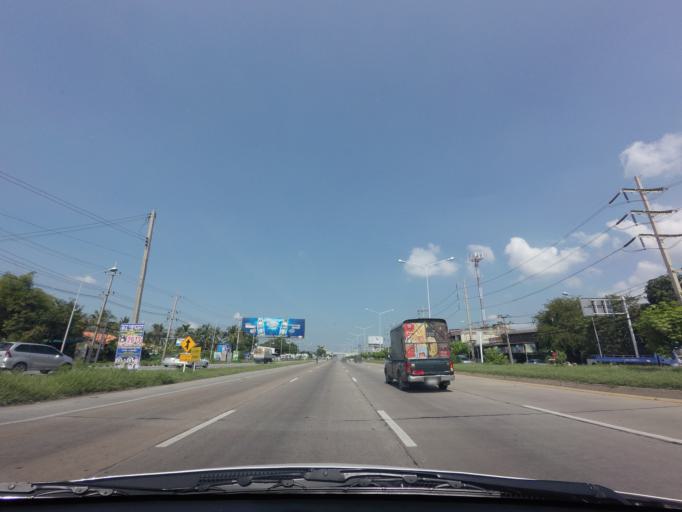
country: TH
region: Nakhon Pathom
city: Nakhon Chai Si
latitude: 13.7671
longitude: 100.1833
